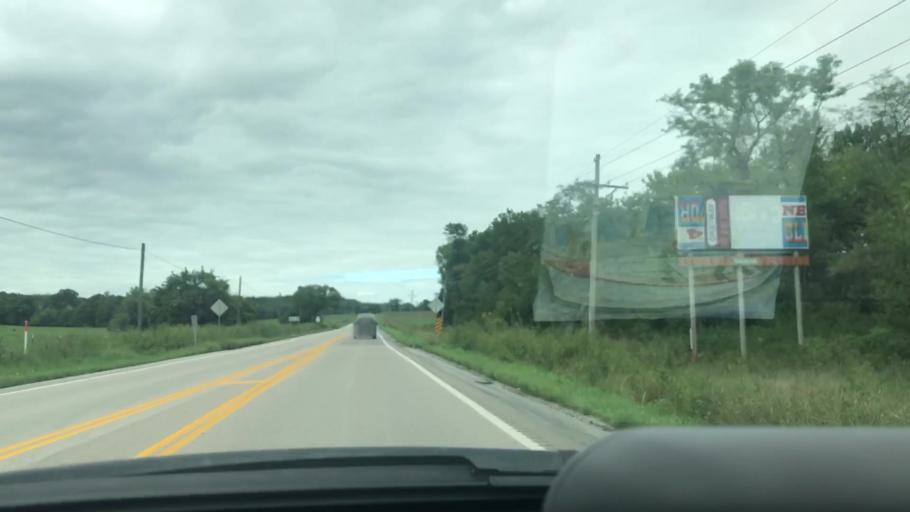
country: US
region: Missouri
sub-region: Hickory County
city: Hermitage
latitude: 37.8614
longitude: -93.1776
